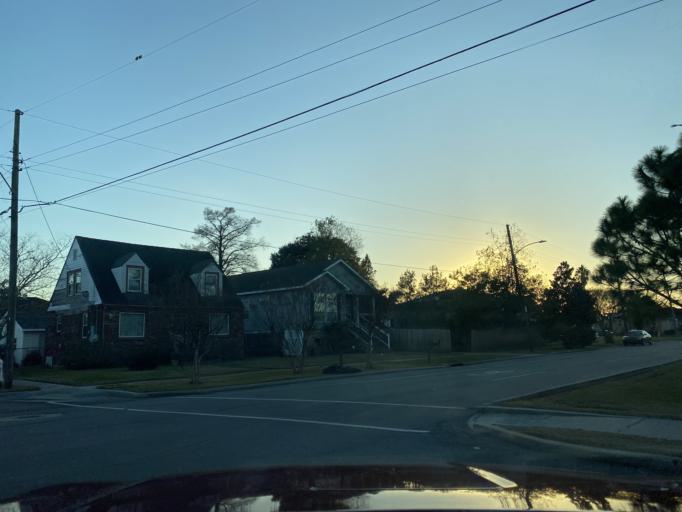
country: US
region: Louisiana
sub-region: Orleans Parish
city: New Orleans
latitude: 30.0222
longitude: -90.0575
